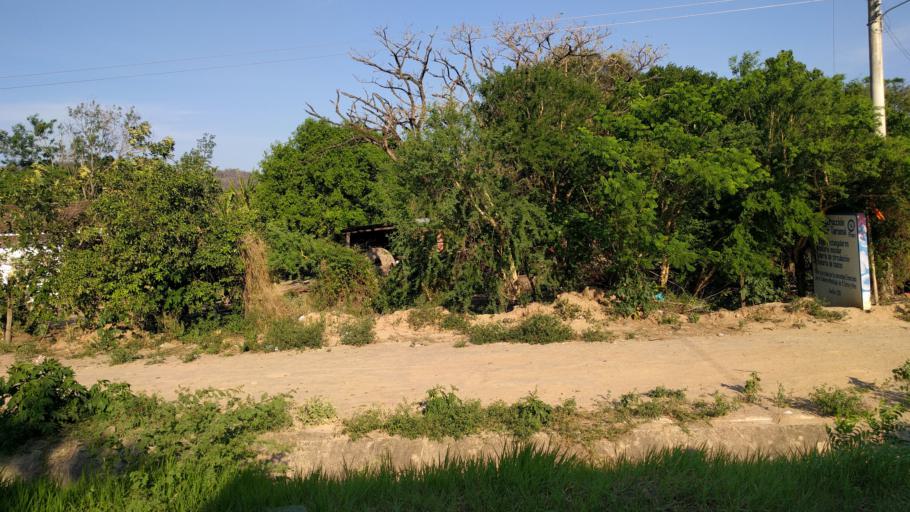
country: BO
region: Santa Cruz
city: Jorochito
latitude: -18.1170
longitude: -63.4612
